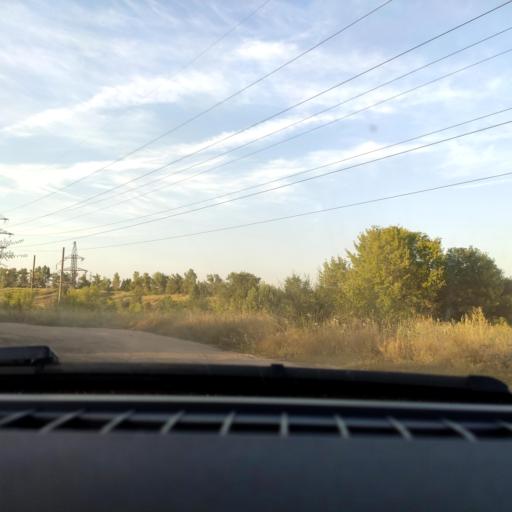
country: RU
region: Voronezj
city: Maslovka
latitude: 51.6140
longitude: 39.2723
